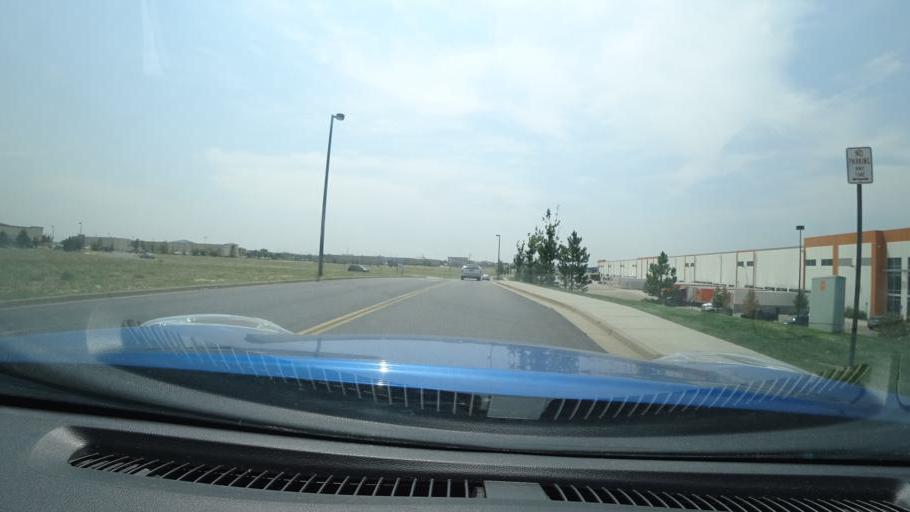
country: US
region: Colorado
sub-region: Adams County
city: Aurora
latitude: 39.7690
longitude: -104.7744
